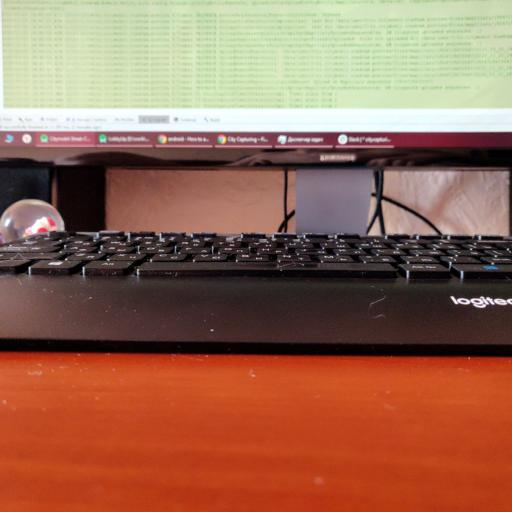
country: EE
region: Hiiumaa
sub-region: Kaerdla linn
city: Kardla
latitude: 59.0940
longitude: 22.8134
